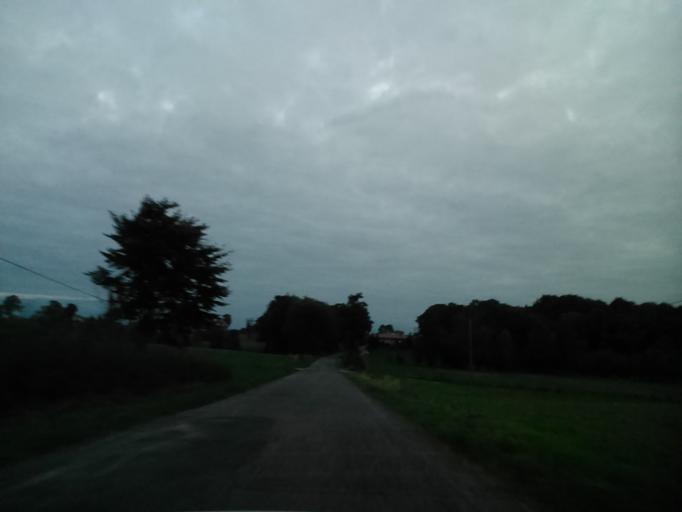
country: PL
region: Kujawsko-Pomorskie
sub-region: Powiat golubsko-dobrzynski
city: Kowalewo Pomorskie
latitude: 53.1189
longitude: 18.9070
